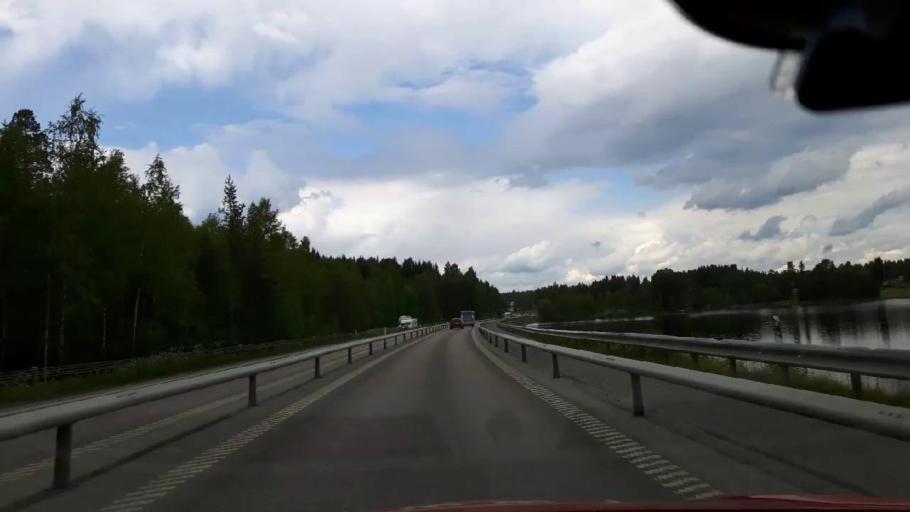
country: SE
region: Jaemtland
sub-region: Krokoms Kommun
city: Krokom
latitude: 63.3219
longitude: 14.4387
